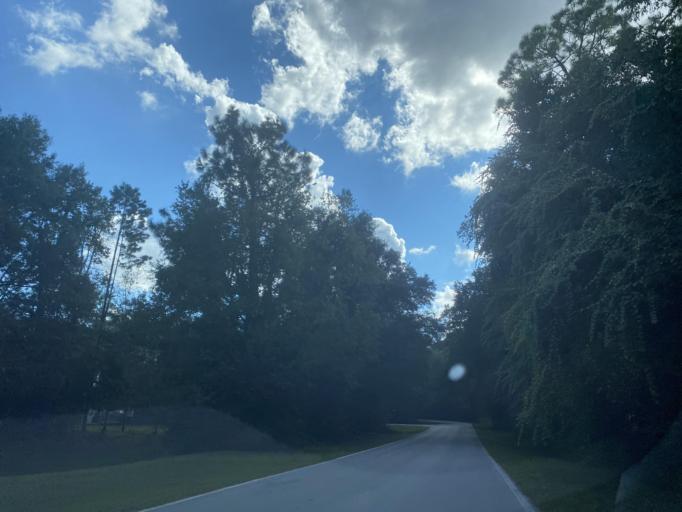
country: US
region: Florida
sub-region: Marion County
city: Ocala
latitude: 29.0561
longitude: -82.2539
